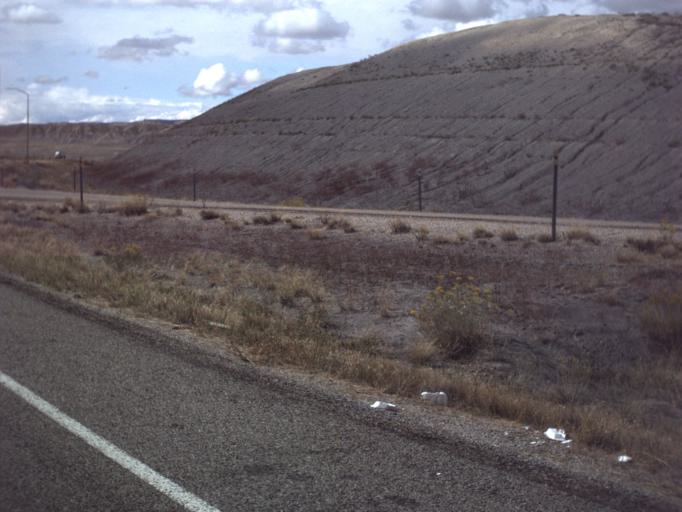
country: US
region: Utah
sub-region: Grand County
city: Moab
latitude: 38.9509
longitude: -109.6861
